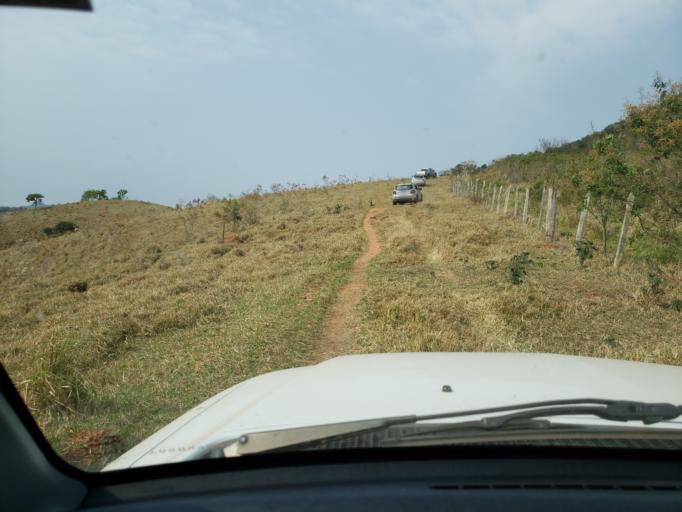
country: BR
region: Minas Gerais
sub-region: Jacutinga
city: Jacutinga
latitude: -22.3435
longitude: -46.5871
